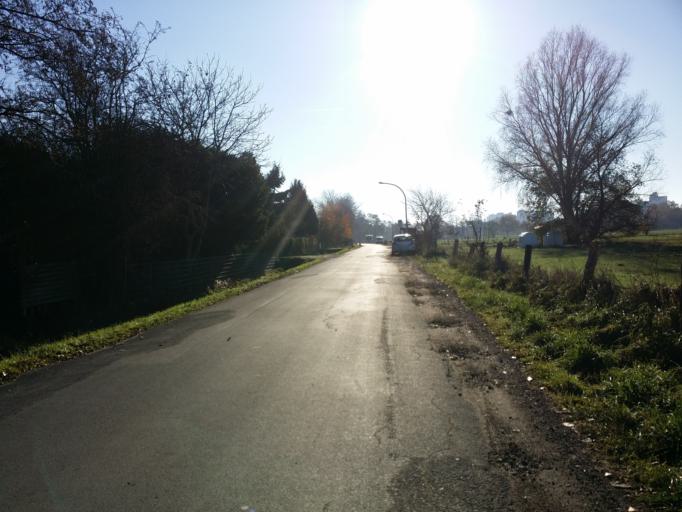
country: DE
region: Lower Saxony
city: Oyten
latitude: 53.0772
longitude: 8.9670
